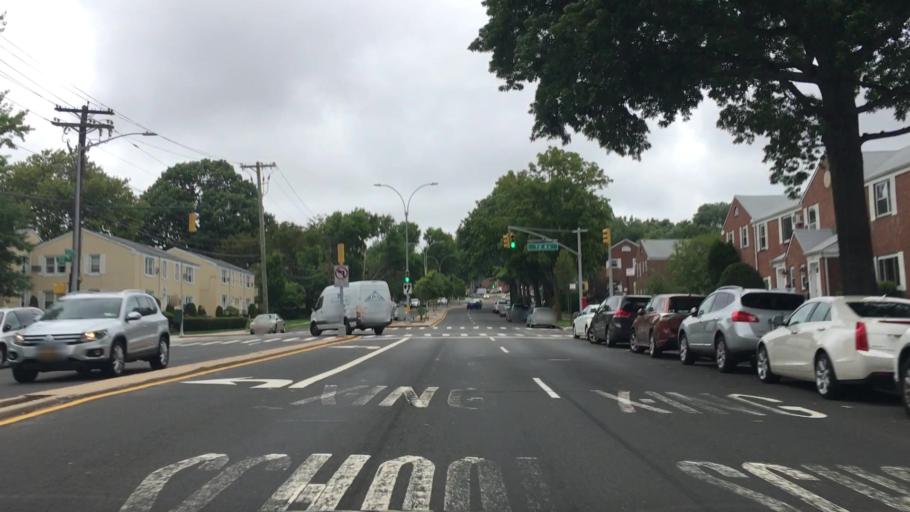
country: US
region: New York
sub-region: Nassau County
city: Lake Success
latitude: 40.7501
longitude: -73.7202
